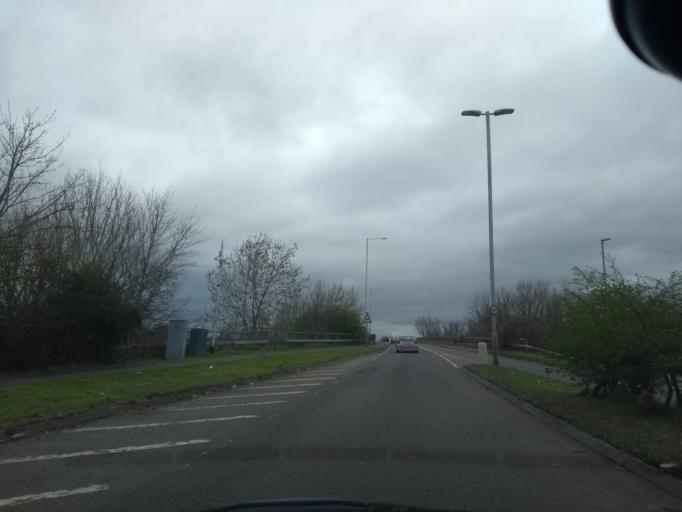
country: GB
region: England
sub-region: Somerset
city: Taunton
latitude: 51.0222
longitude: -3.0903
